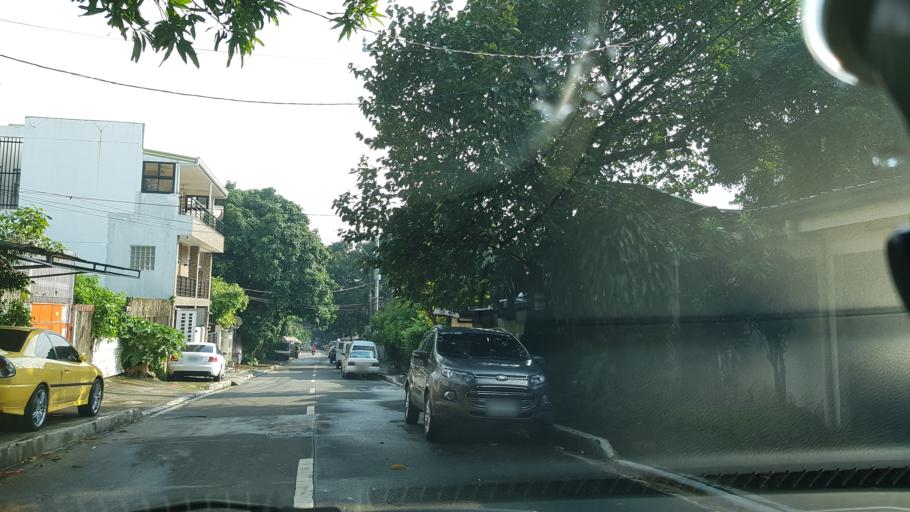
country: PH
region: Metro Manila
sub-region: Quezon City
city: Quezon City
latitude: 14.6351
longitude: 121.0482
